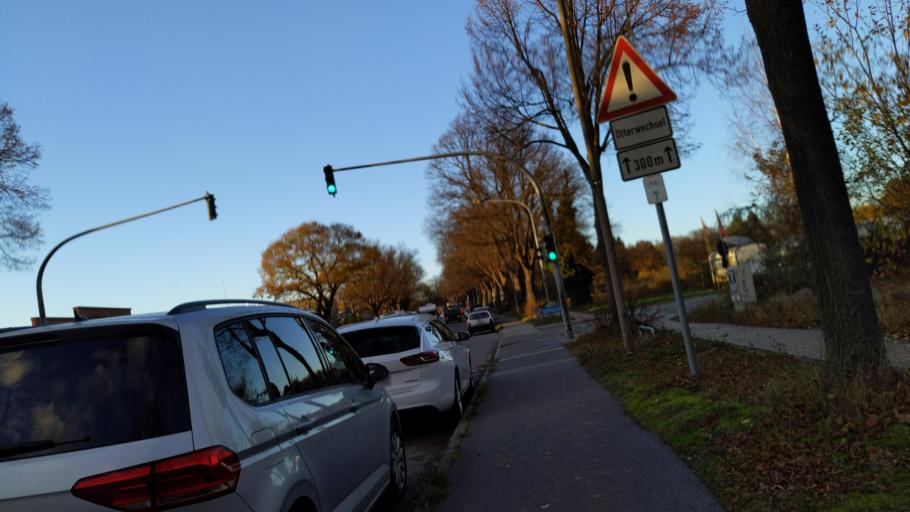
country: DE
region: Schleswig-Holstein
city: Luebeck
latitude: 53.8721
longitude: 10.6978
